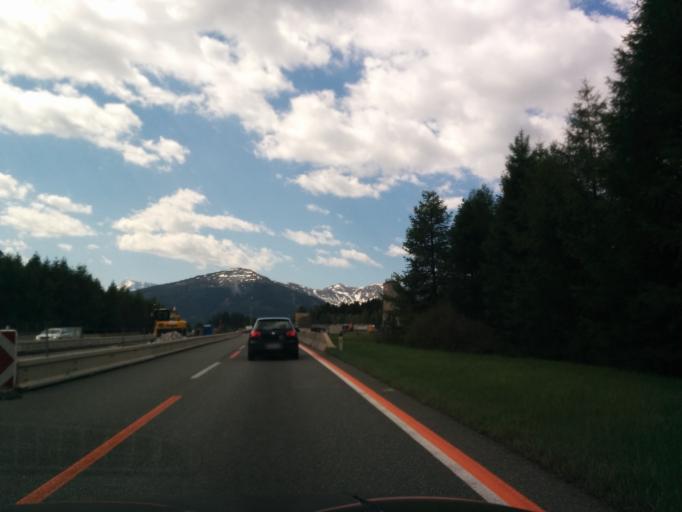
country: AT
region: Tyrol
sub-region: Politischer Bezirk Innsbruck Land
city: Gries am Brenner
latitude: 47.0667
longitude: 11.4876
